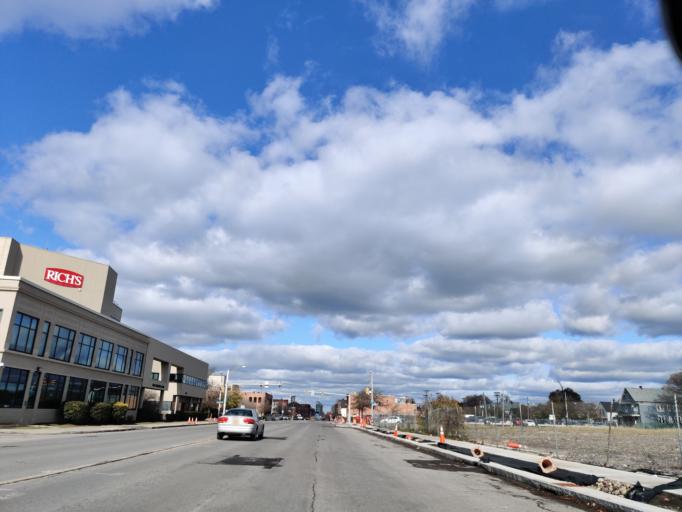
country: US
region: New York
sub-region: Erie County
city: Buffalo
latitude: 42.9143
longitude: -78.8995
